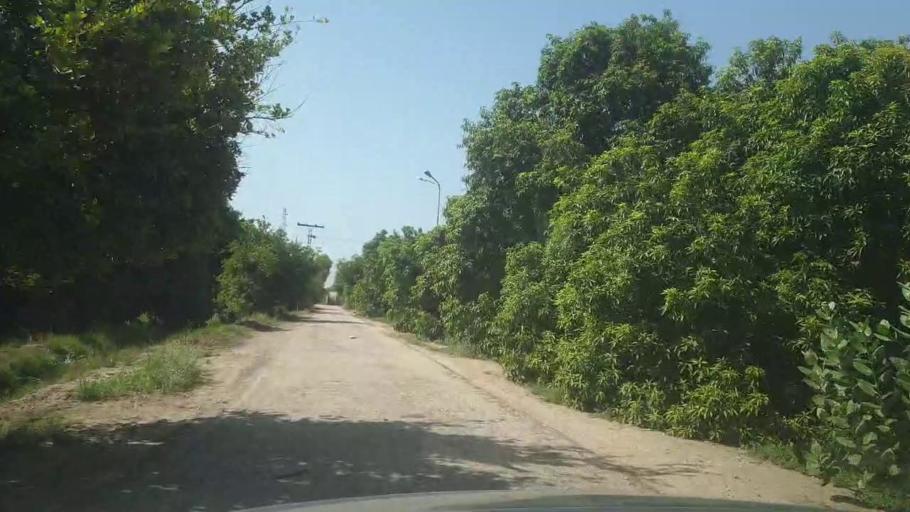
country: PK
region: Sindh
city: Rohri
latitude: 27.4080
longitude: 69.0806
